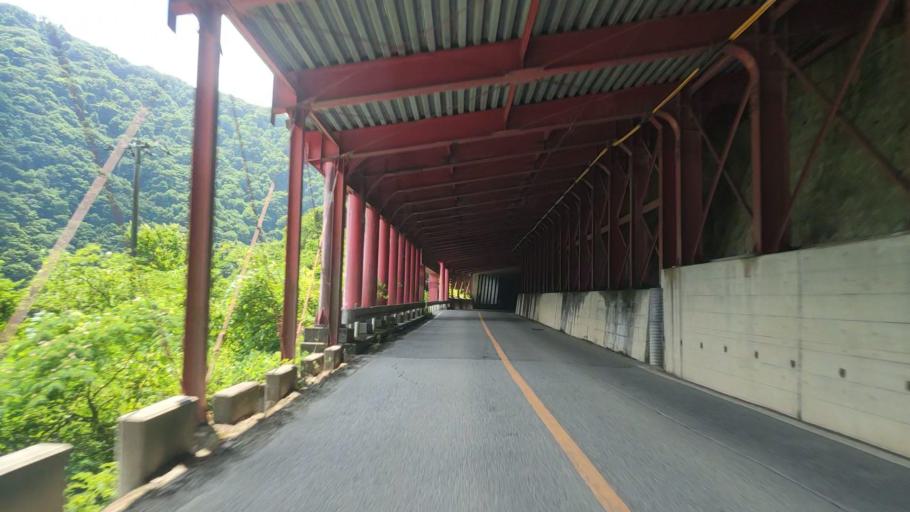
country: JP
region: Fukui
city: Ono
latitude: 35.9241
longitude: 136.5456
